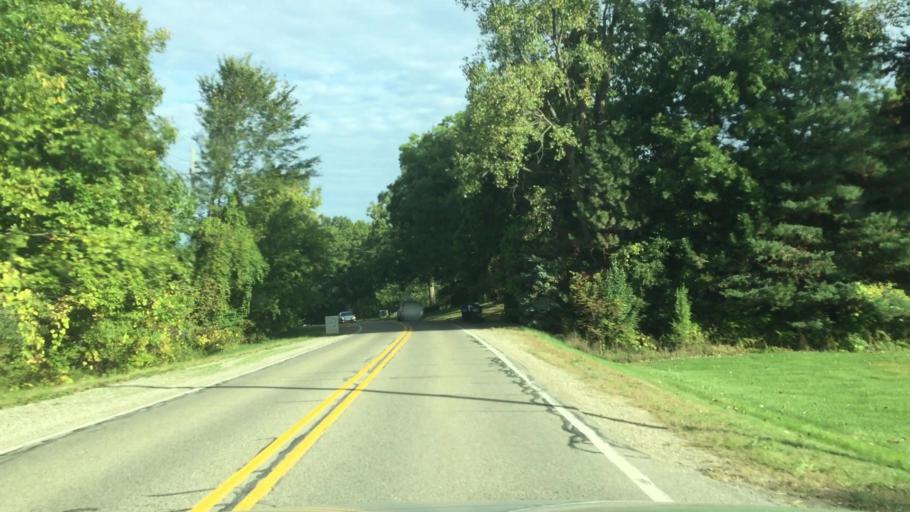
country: US
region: Michigan
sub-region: Livingston County
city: Howell
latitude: 42.5916
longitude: -83.9013
